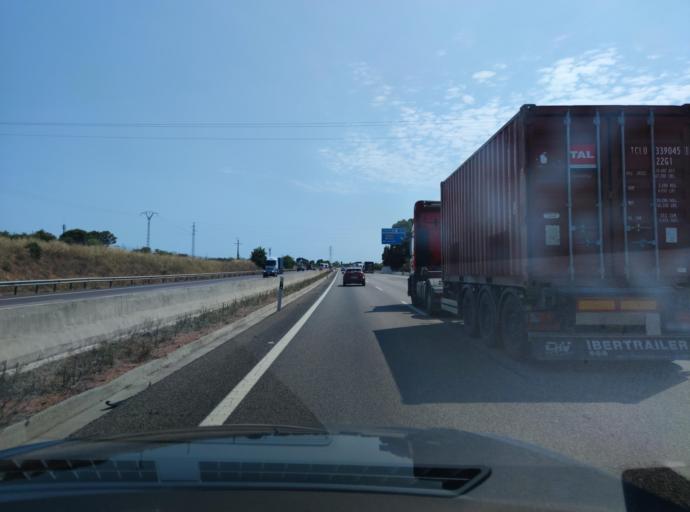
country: ES
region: Valencia
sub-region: Provincia de Valencia
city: Betera
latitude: 39.5722
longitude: -0.4231
